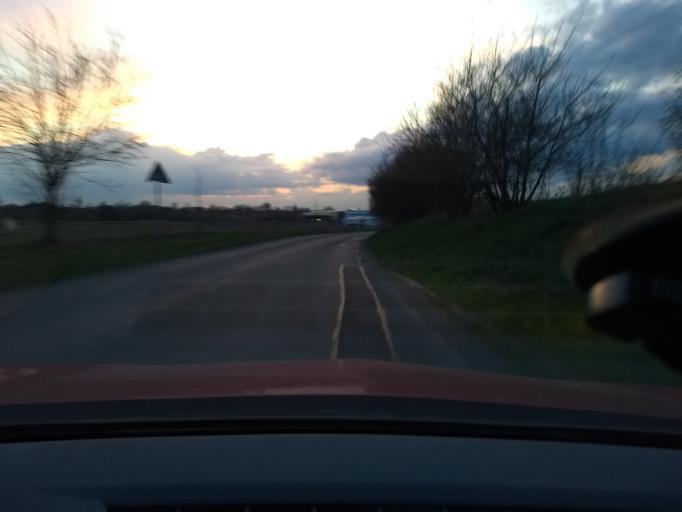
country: CZ
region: Central Bohemia
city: Rudna
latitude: 50.0601
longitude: 14.2422
